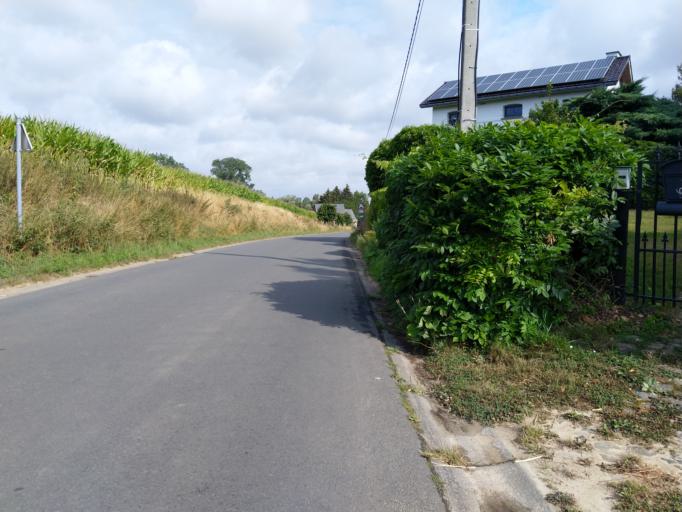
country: BE
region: Wallonia
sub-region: Province du Hainaut
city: Chievres
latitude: 50.5955
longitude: 3.8035
